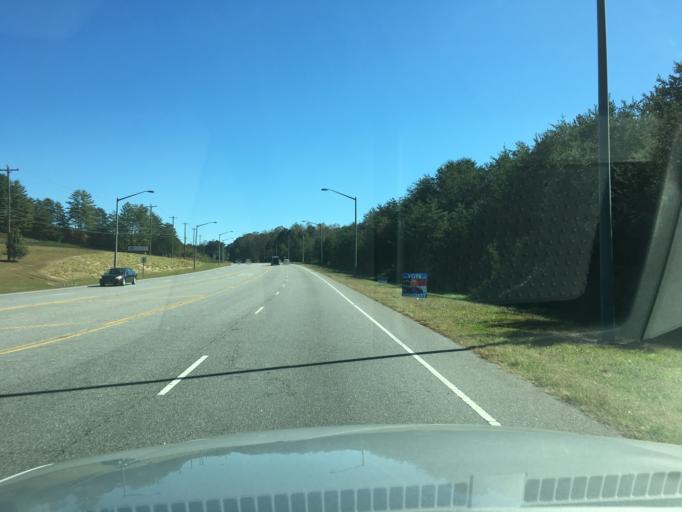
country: US
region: North Carolina
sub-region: Catawba County
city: Saint Stephens
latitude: 35.7194
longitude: -81.2762
